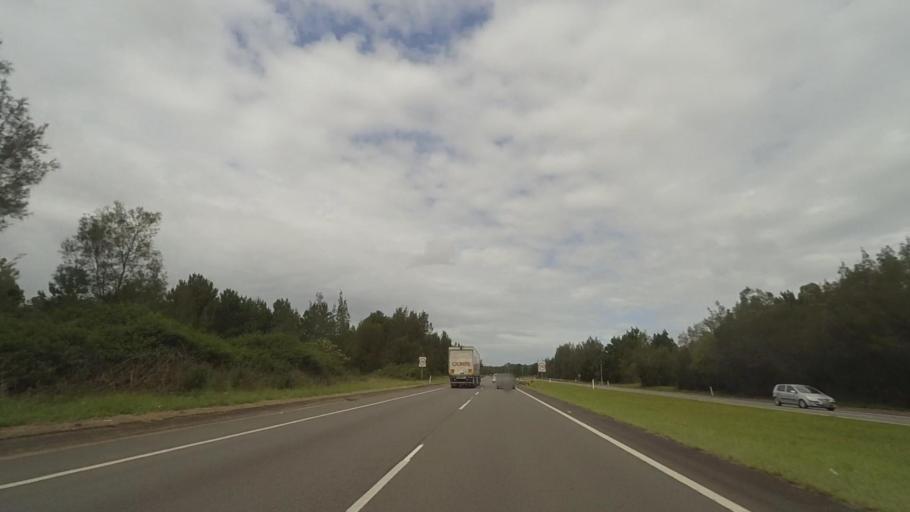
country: AU
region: New South Wales
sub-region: Port Stephens Shire
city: Raymond Terrace
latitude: -32.7793
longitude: 151.7474
